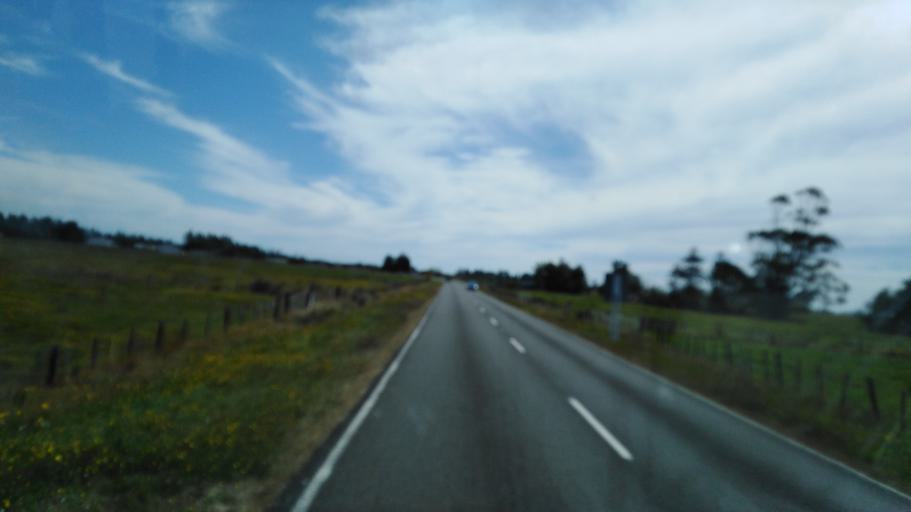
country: NZ
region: West Coast
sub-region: Buller District
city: Westport
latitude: -41.7581
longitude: 171.6419
